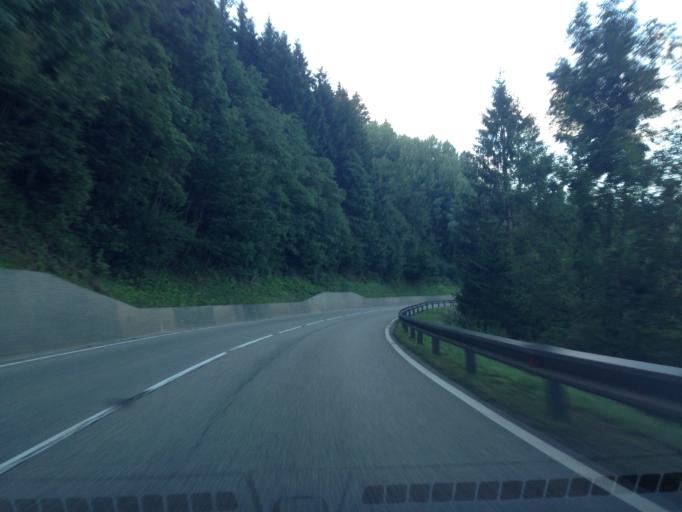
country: AT
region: Tyrol
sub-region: Politischer Bezirk Reutte
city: Breitenwang
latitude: 47.4751
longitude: 10.7285
